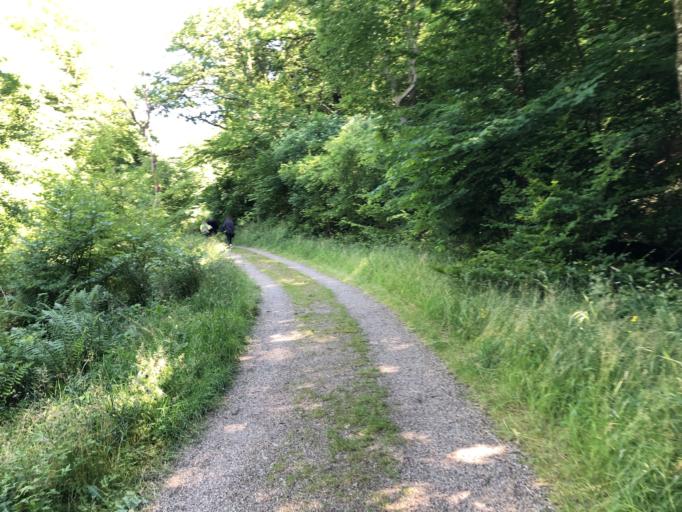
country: DK
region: Central Jutland
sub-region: Viborg Kommune
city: Stoholm
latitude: 56.4428
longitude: 9.1406
